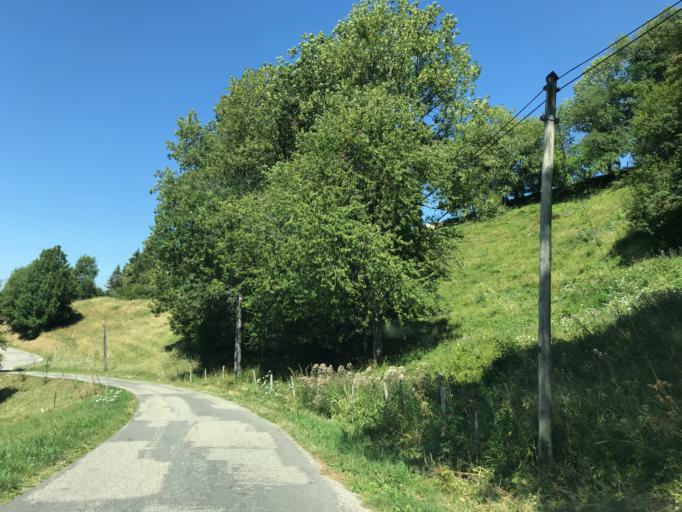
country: FR
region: Rhone-Alpes
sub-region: Departement de la Haute-Savoie
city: Thorens-Glieres
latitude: 45.9781
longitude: 6.2308
